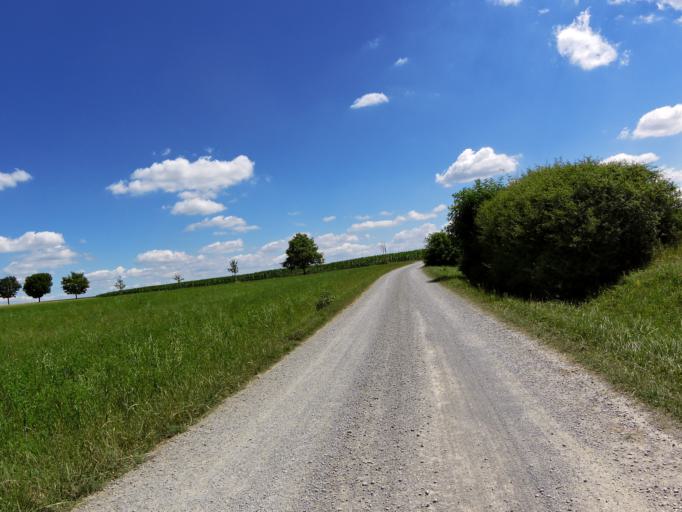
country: DE
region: Bavaria
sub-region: Regierungsbezirk Unterfranken
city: Wuerzburg
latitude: 49.8252
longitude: 9.9388
